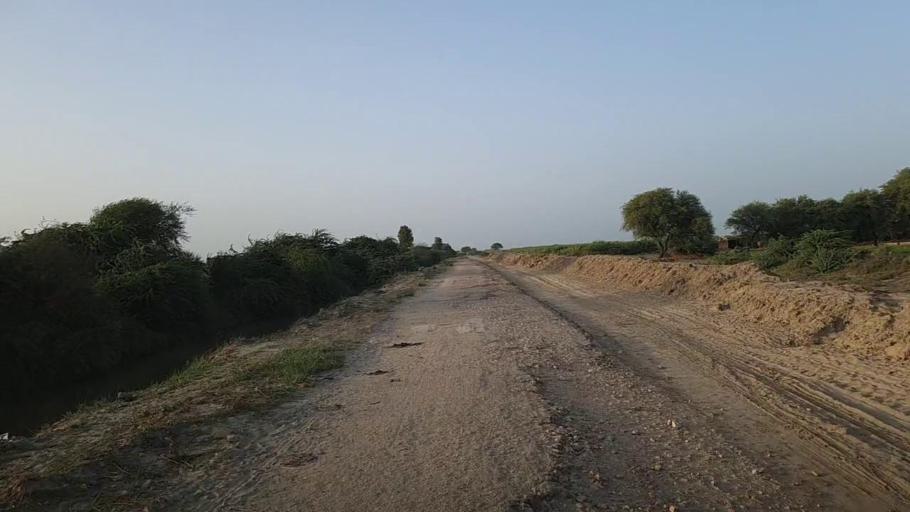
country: PK
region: Sindh
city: Kario
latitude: 24.7032
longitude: 68.4649
